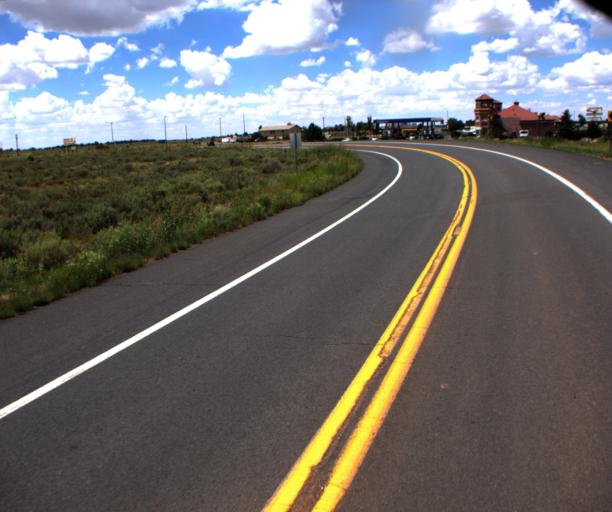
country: US
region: Arizona
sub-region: Coconino County
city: Grand Canyon Village
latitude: 35.6514
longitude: -112.1372
